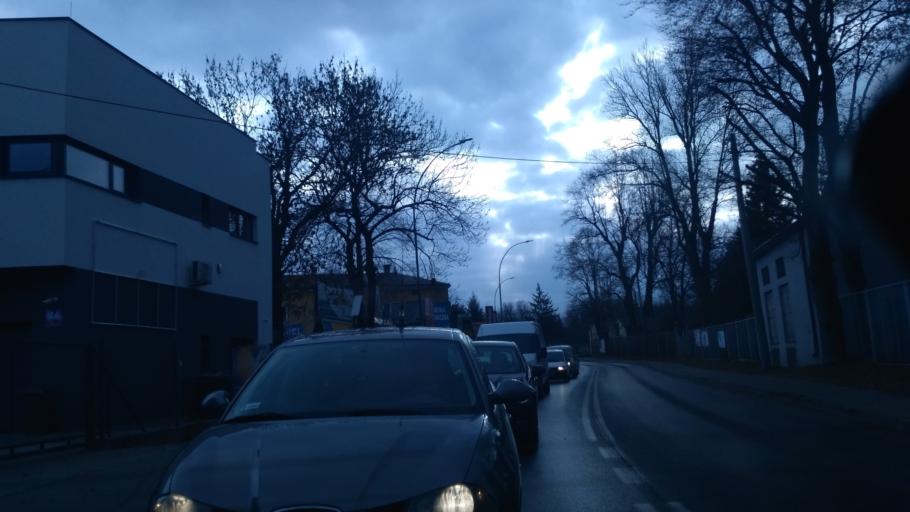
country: PL
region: Subcarpathian Voivodeship
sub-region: Powiat lancucki
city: Lancut
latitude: 50.0805
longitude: 22.2330
